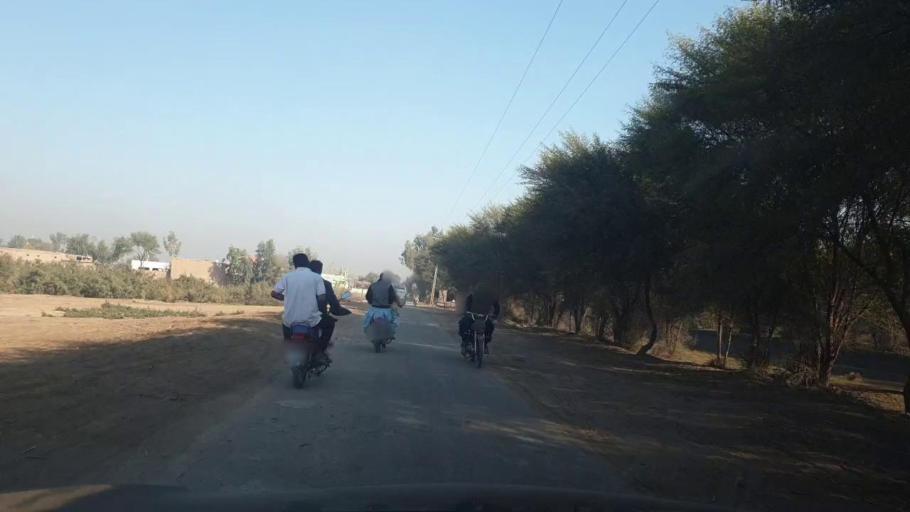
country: PK
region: Sindh
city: Mirpur Mathelo
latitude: 28.0714
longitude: 69.4671
